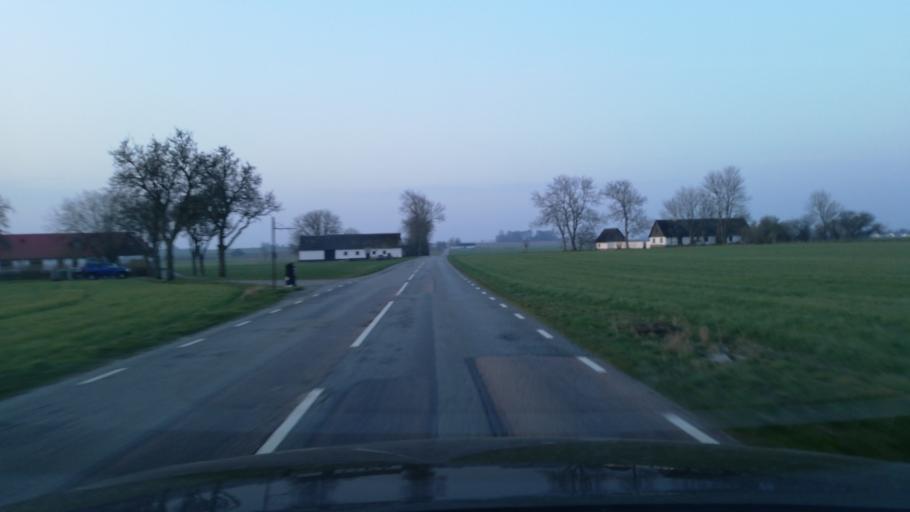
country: SE
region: Skane
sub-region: Tomelilla Kommun
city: Tomelilla
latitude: 55.4807
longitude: 14.1007
